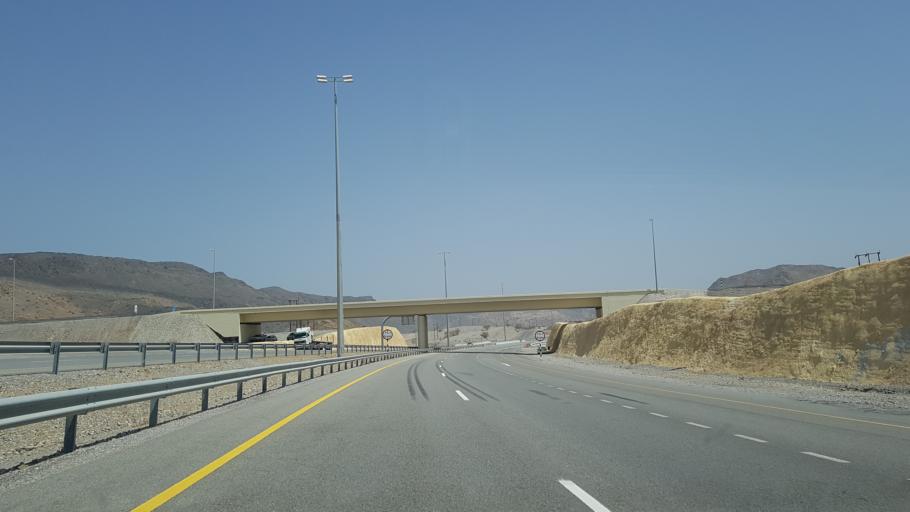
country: OM
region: Muhafazat Masqat
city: Muscat
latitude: 23.2469
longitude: 58.7893
